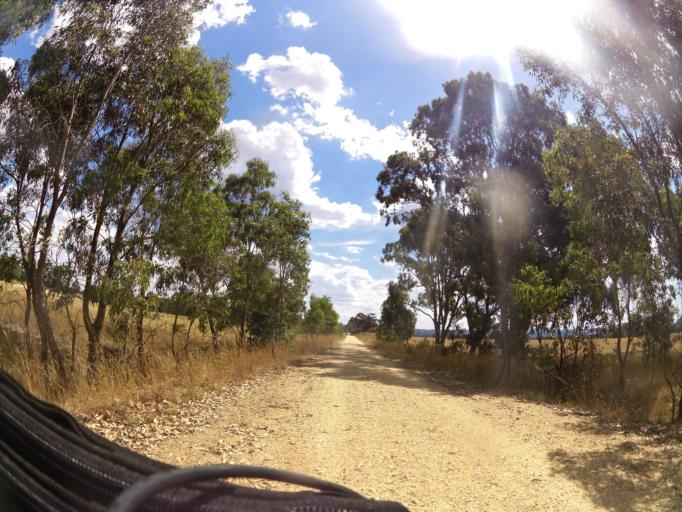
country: AU
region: Victoria
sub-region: Wellington
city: Heyfield
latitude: -37.9779
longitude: 146.7525
